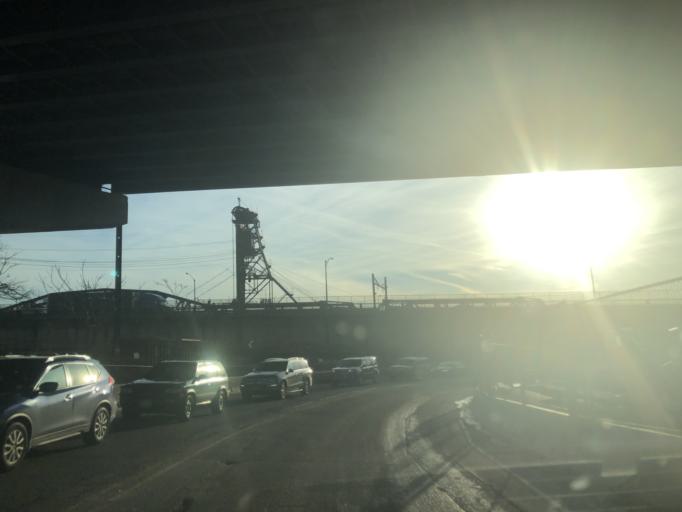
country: US
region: New Jersey
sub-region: Hudson County
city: Jersey City
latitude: 40.7423
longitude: -74.0829
